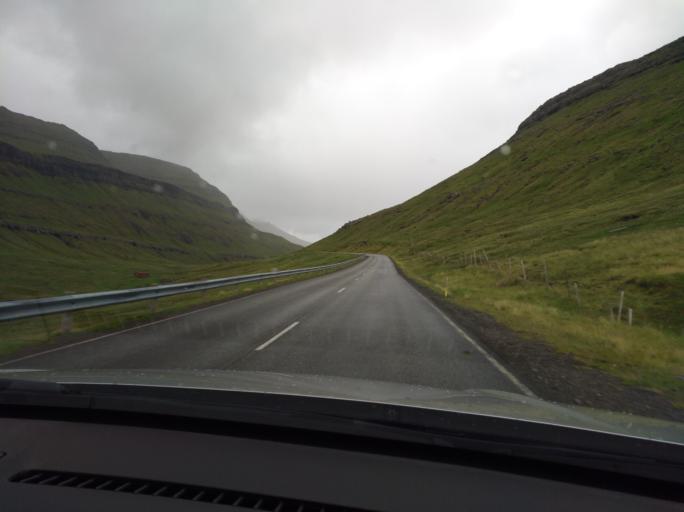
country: FO
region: Eysturoy
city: Fuglafjordur
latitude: 62.2274
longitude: -6.8791
